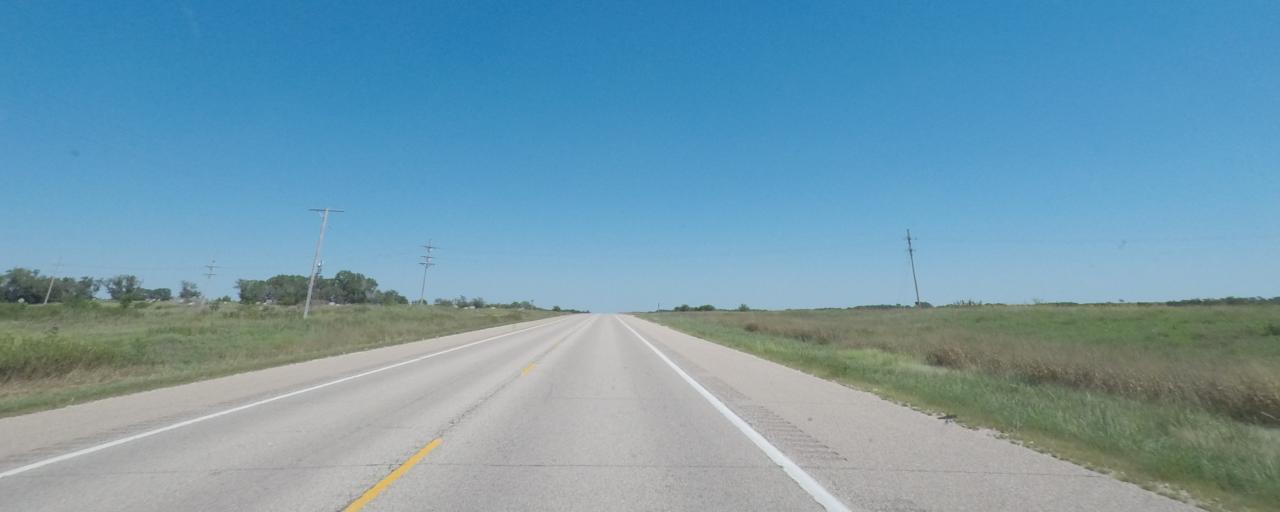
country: US
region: Kansas
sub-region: Marion County
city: Peabody
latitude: 38.2051
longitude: -97.0070
